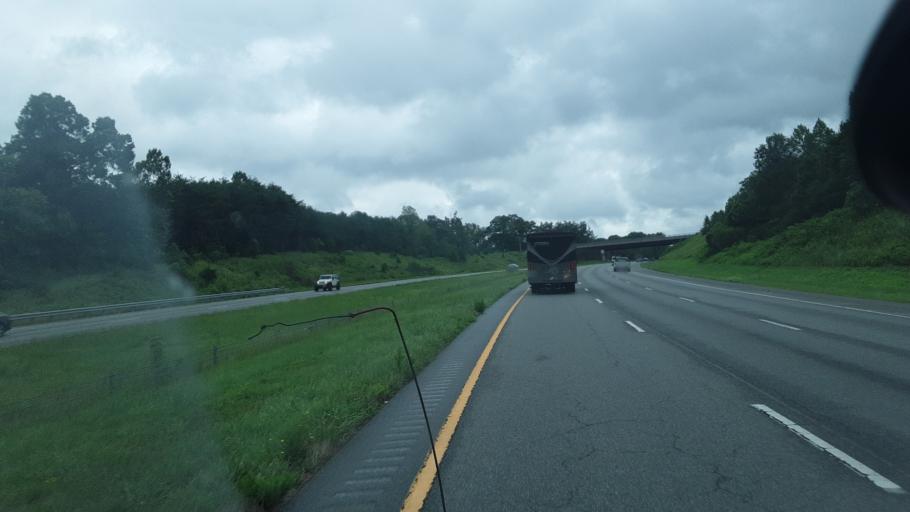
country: US
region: North Carolina
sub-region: Randolph County
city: Archdale
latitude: 35.9369
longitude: -79.9396
